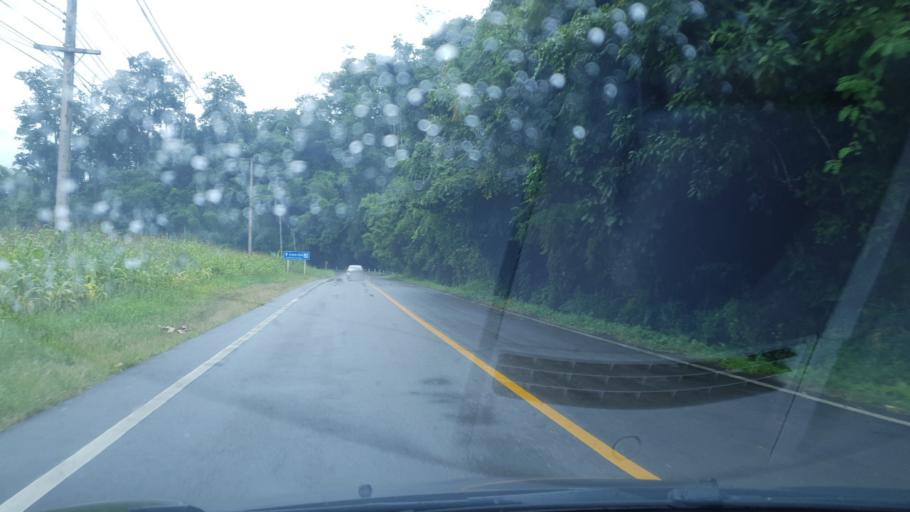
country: TH
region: Mae Hong Son
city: Mae La Noi
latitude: 18.5761
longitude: 97.9379
